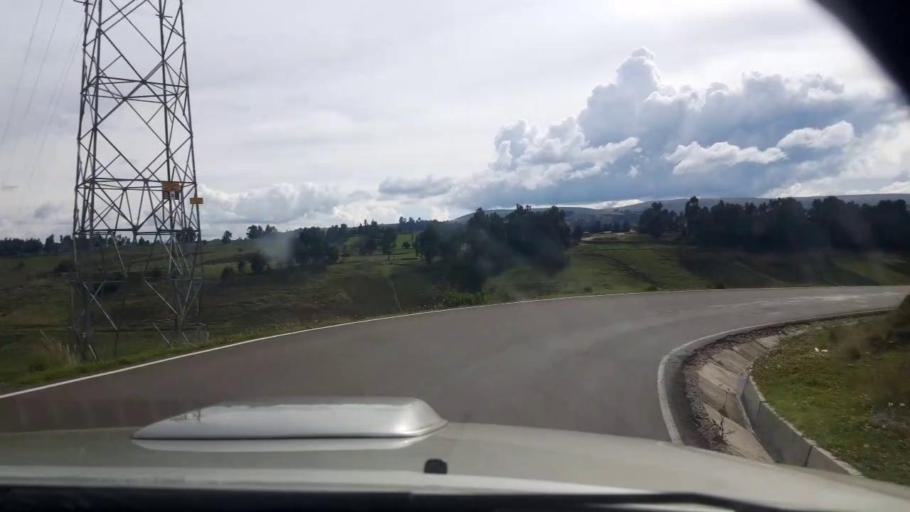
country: PE
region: Ayacucho
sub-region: Provincia de Cangallo
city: Pampa Cangallo
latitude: -13.4509
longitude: -74.1991
